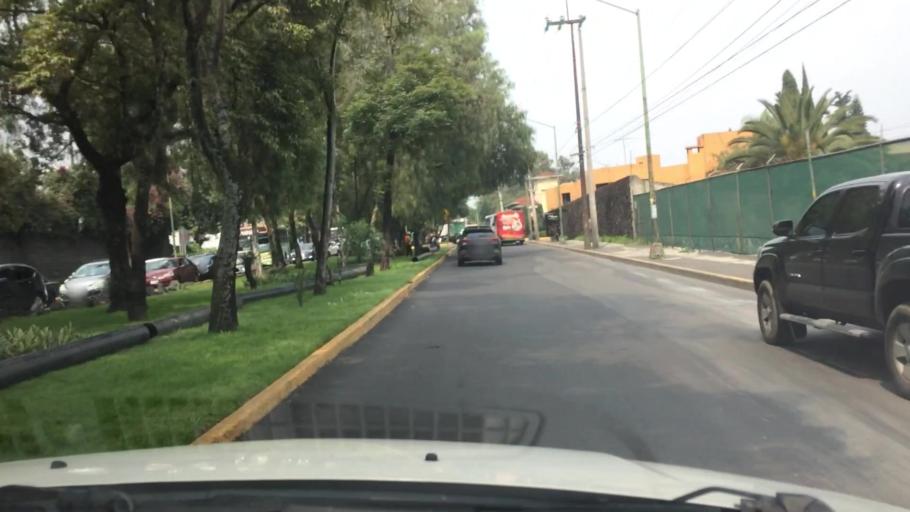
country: MX
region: Mexico City
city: Magdalena Contreras
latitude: 19.3089
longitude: -99.2044
